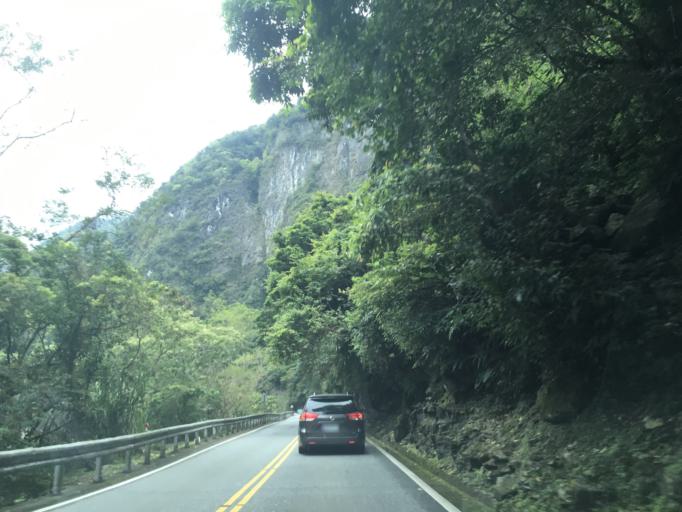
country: TW
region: Taiwan
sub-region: Hualien
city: Hualian
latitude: 24.1689
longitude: 121.6030
